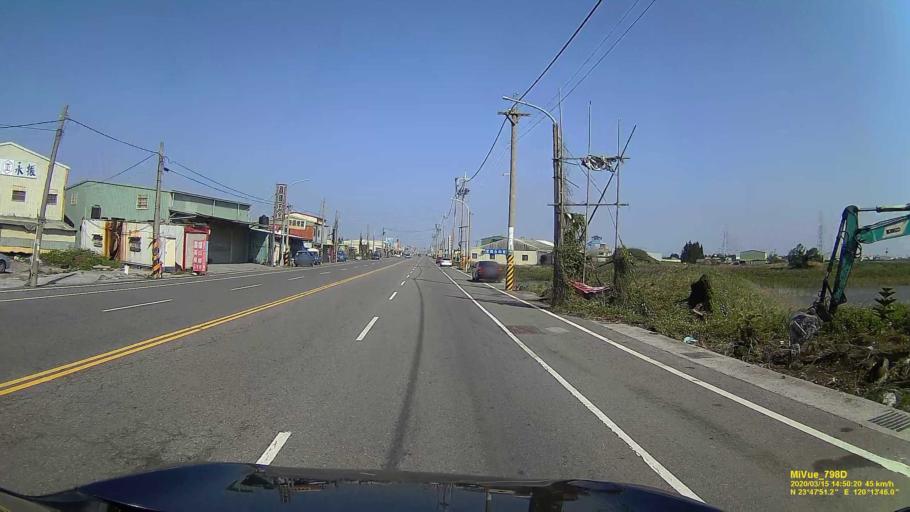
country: TW
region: Taiwan
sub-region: Yunlin
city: Douliu
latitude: 23.7976
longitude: 120.2295
